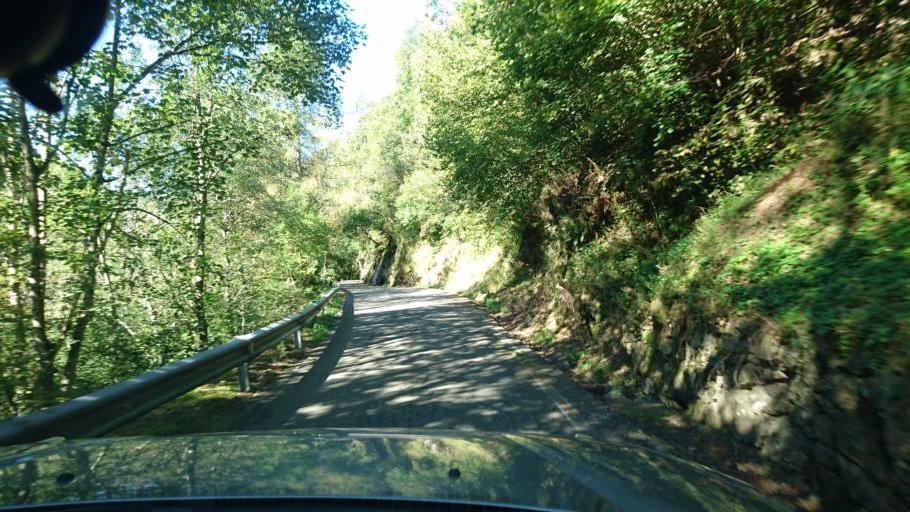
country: IT
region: Lombardy
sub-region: Provincia di Brescia
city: Paisco Loveno
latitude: 46.0616
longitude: 10.2502
